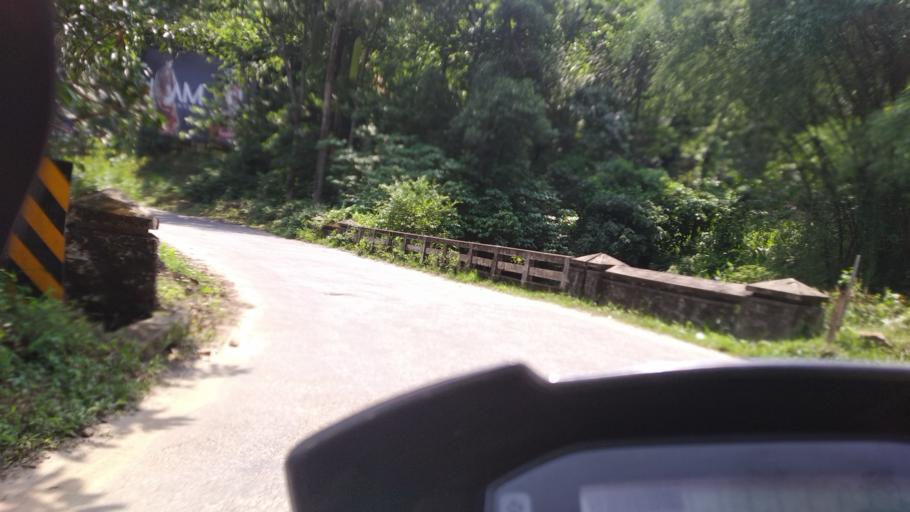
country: IN
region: Kerala
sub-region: Kottayam
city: Erattupetta
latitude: 9.6927
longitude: 76.8712
